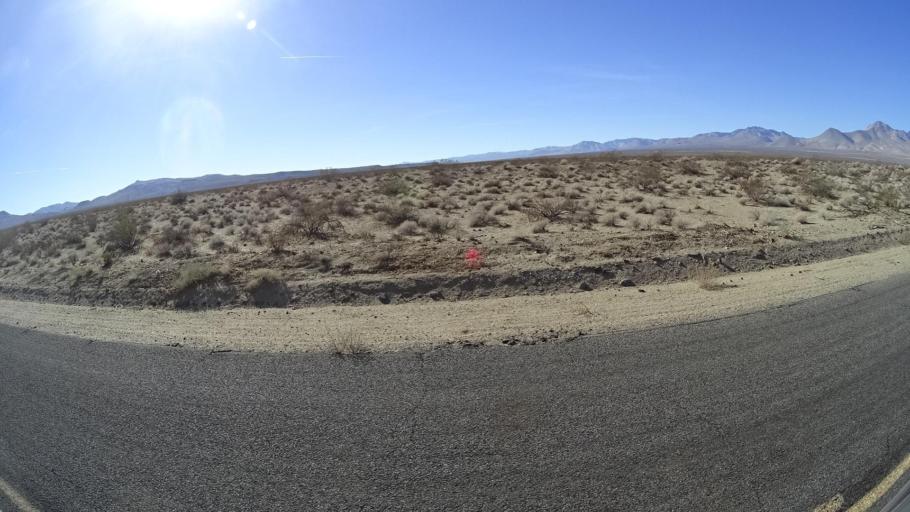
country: US
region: California
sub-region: Kern County
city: China Lake Acres
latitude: 35.5892
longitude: -117.7925
